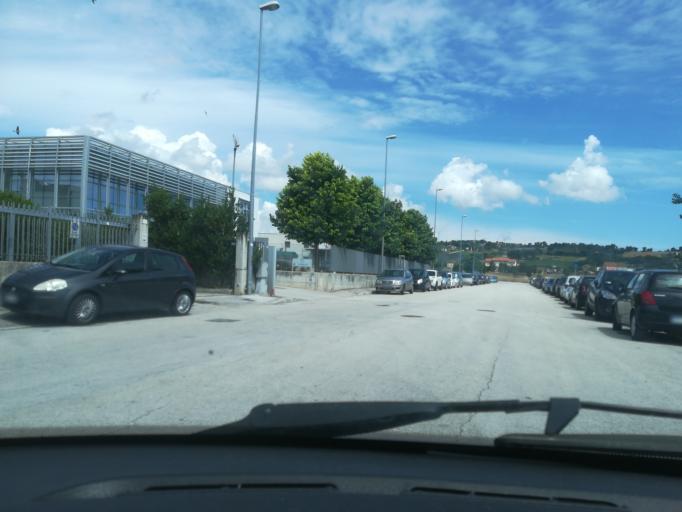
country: IT
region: The Marches
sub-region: Provincia di Macerata
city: Santa Maria Apparente
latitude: 43.2874
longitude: 13.6798
